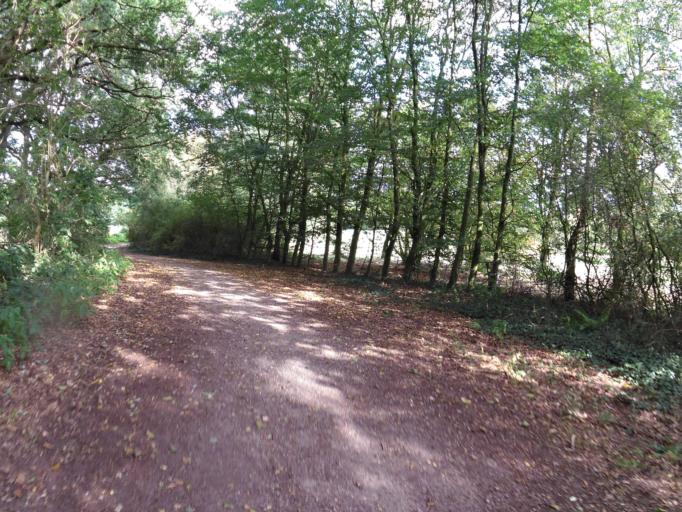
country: DE
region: Lower Saxony
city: Sittensen
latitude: 53.2755
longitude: 9.4856
